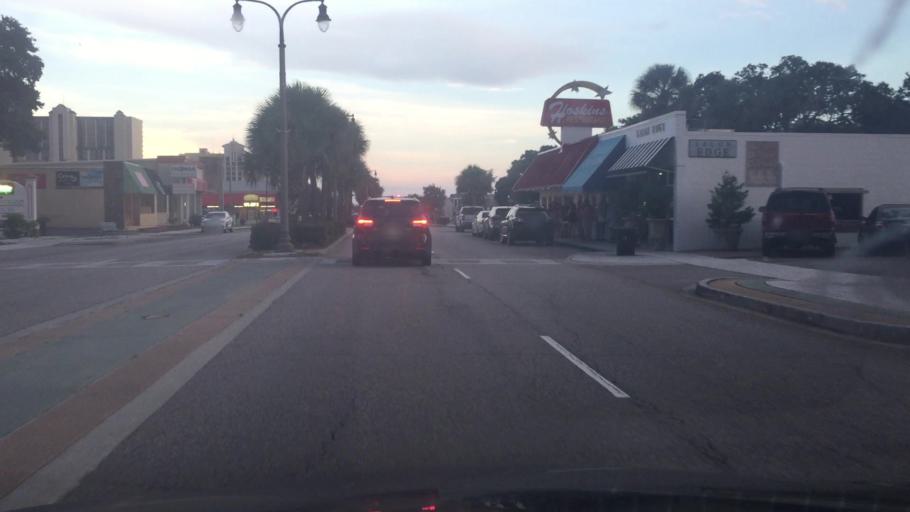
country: US
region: South Carolina
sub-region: Horry County
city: North Myrtle Beach
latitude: 33.8225
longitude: -78.6744
